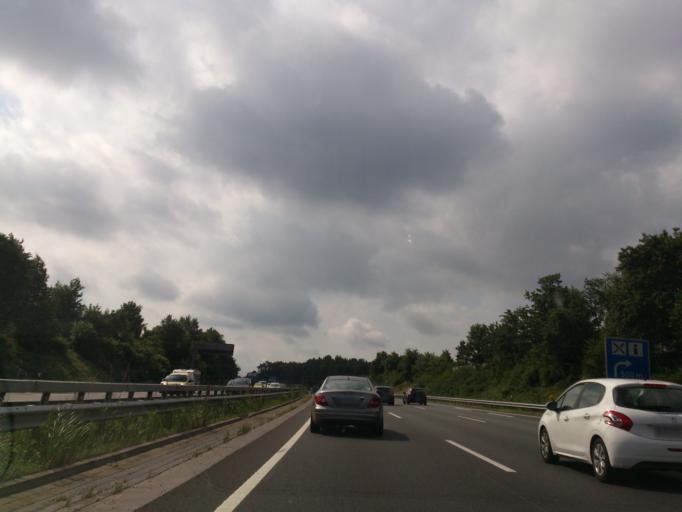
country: DE
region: Lower Saxony
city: Marxen
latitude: 53.3395
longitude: 10.0391
